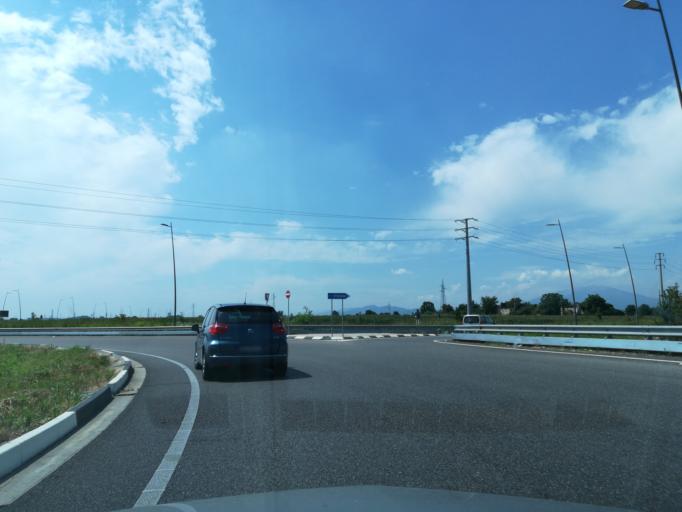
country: IT
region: Lombardy
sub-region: Provincia di Bergamo
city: Comun Nuovo
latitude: 45.6332
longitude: 9.6588
